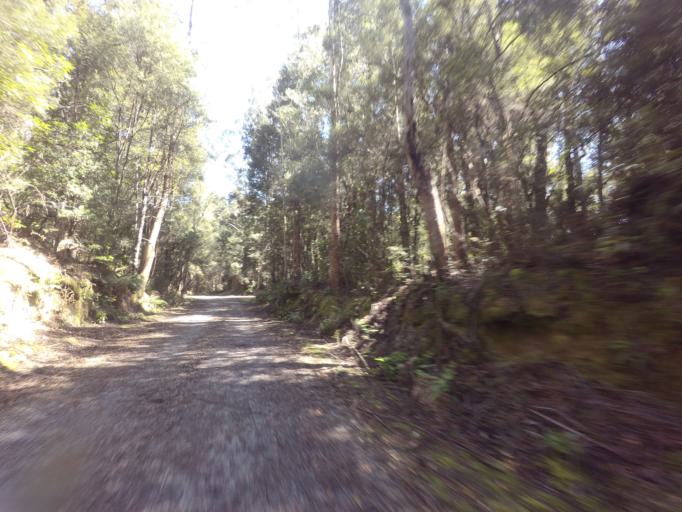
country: AU
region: Tasmania
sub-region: Huon Valley
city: Geeveston
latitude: -43.0380
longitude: 146.3021
